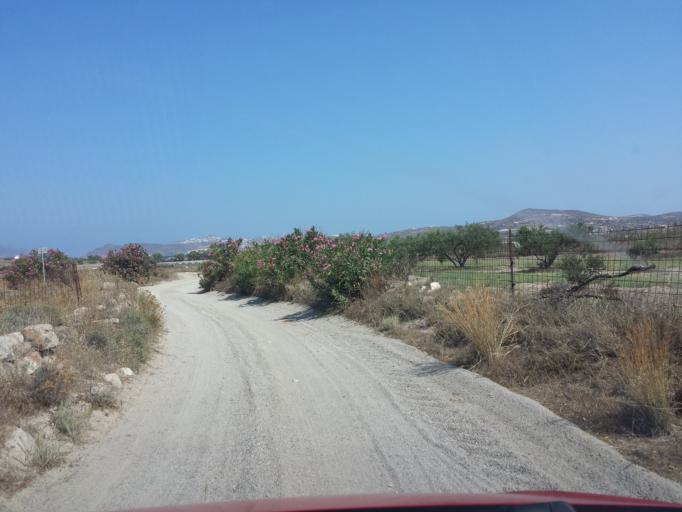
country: GR
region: South Aegean
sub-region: Nomos Kykladon
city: Adamas
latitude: 36.6880
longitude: 24.4883
